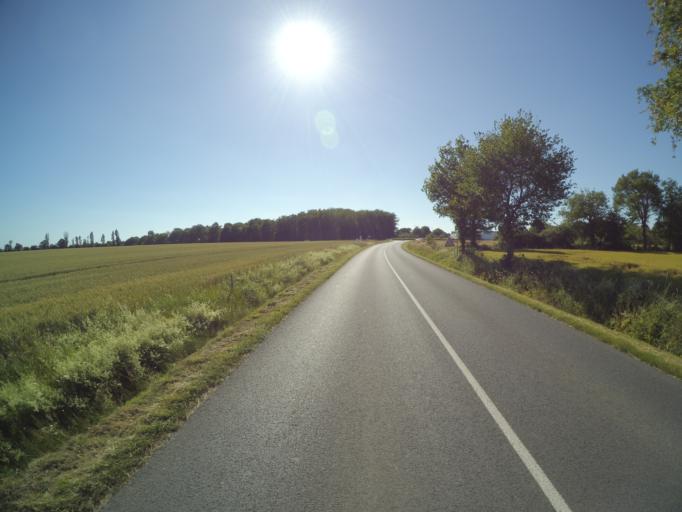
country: FR
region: Pays de la Loire
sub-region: Departement de la Vendee
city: La Guyonniere
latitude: 46.9583
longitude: -1.2484
